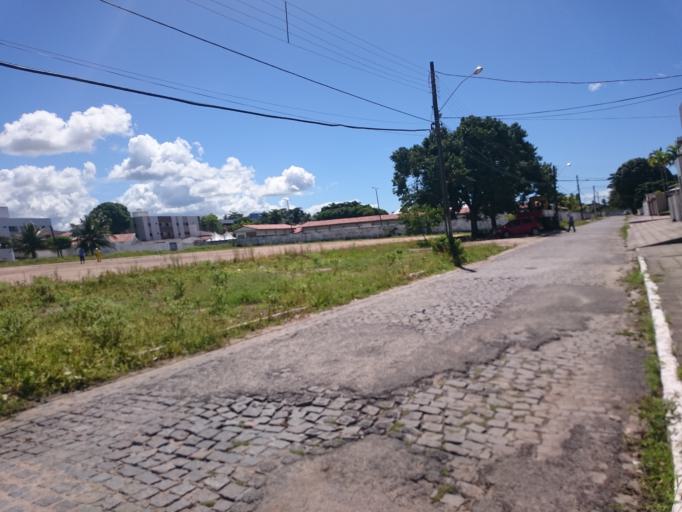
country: BR
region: Paraiba
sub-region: Joao Pessoa
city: Joao Pessoa
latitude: -7.1463
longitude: -34.8430
